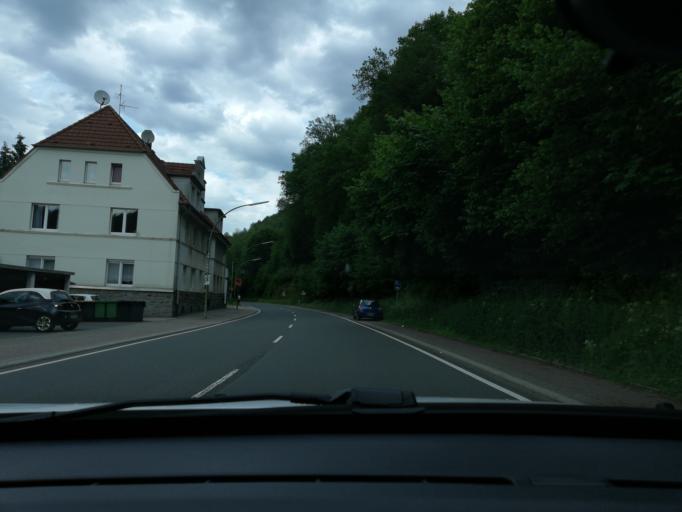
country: DE
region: North Rhine-Westphalia
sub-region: Regierungsbezirk Arnsberg
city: Schalksmuhle
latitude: 51.2532
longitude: 7.5186
